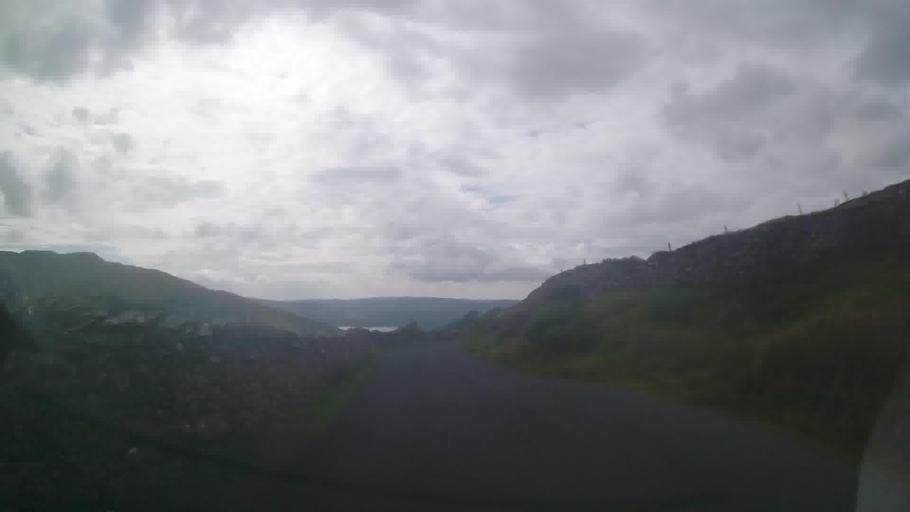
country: GB
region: England
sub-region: Cumbria
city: Ambleside
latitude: 54.4488
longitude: -2.9397
